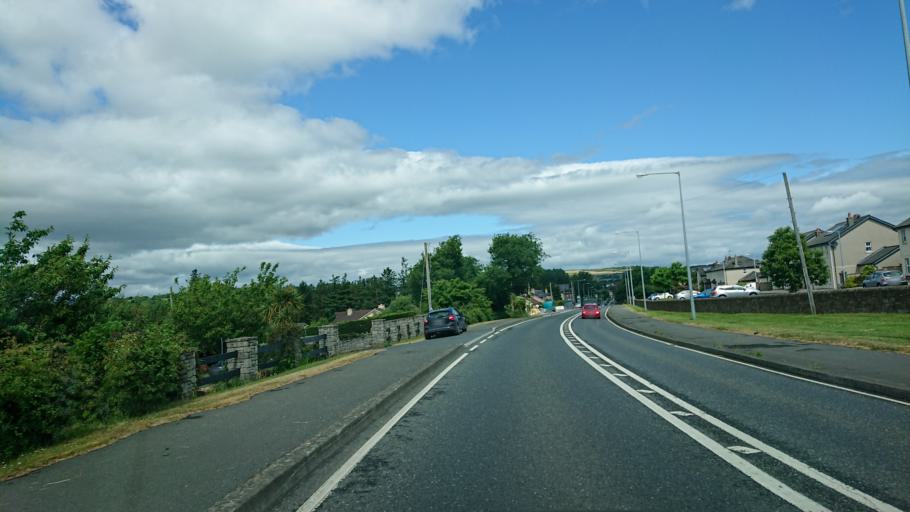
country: IE
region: Leinster
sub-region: Kilkenny
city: Mooncoin
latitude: 52.2286
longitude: -7.2367
